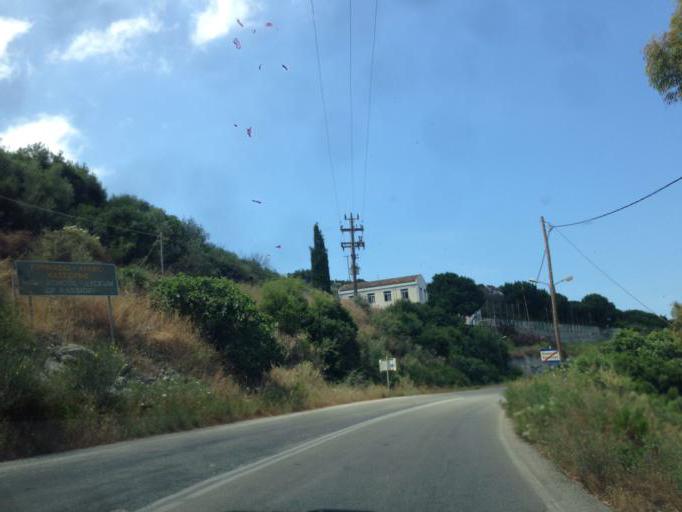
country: GR
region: Ionian Islands
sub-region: Nomos Kerkyras
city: Acharavi
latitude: 39.7885
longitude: 19.9091
